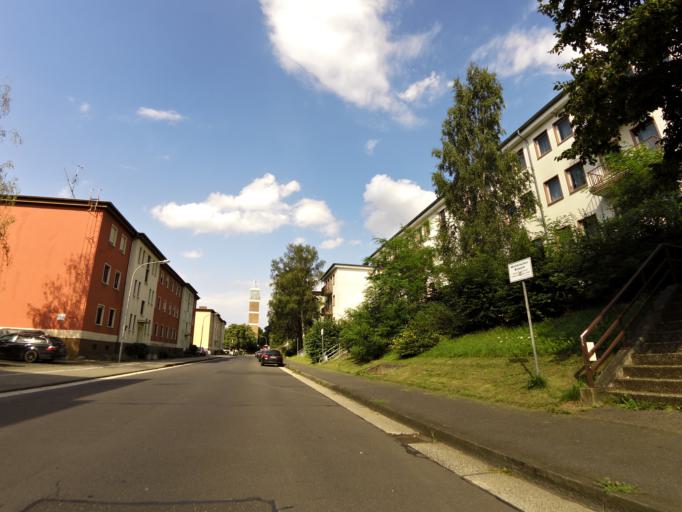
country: DE
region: Rheinland-Pfalz
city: Lahnstein
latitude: 50.3389
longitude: 7.6190
